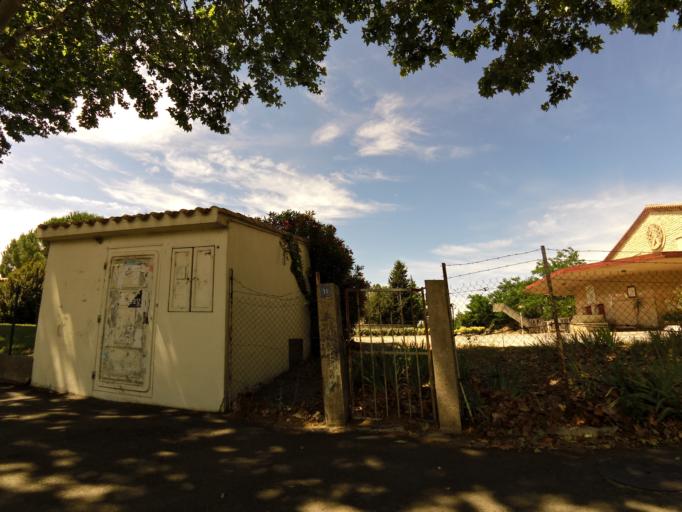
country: FR
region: Languedoc-Roussillon
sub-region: Departement du Gard
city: Bernis
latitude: 43.7692
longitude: 4.2871
